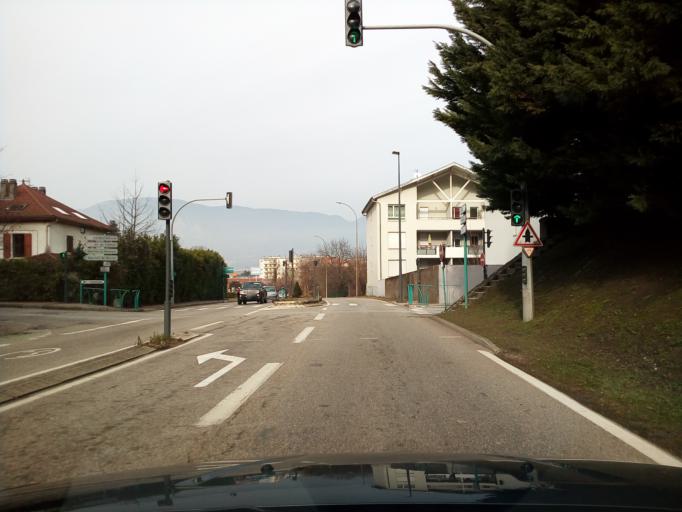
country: FR
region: Rhone-Alpes
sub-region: Departement de l'Isere
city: Gieres
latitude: 45.1789
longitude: 5.7896
